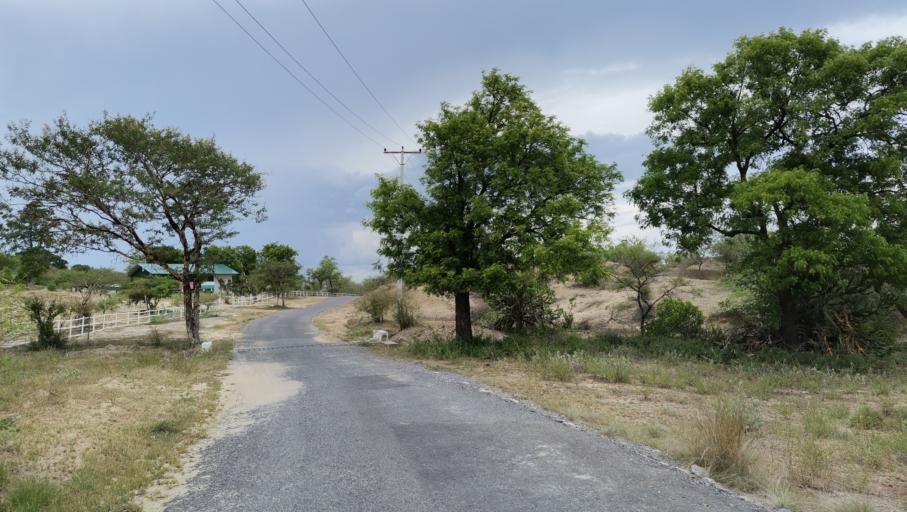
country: MM
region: Mandalay
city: Myingyan
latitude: 21.8223
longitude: 95.3960
